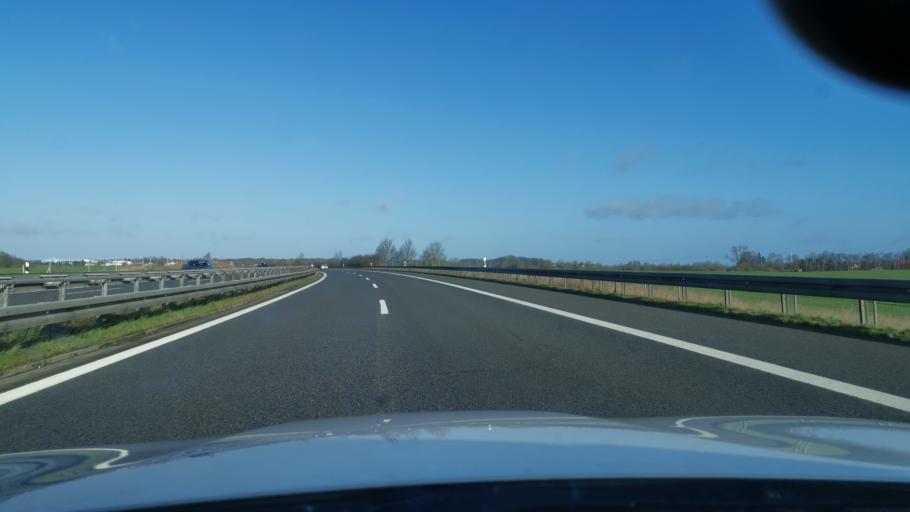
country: DE
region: Mecklenburg-Vorpommern
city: Kritzmow
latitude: 54.0318
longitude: 12.0587
